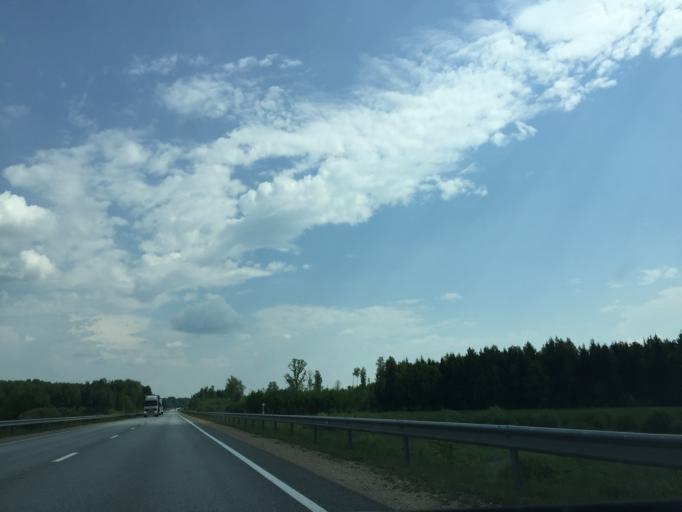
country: LV
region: Lielvarde
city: Lielvarde
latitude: 56.8197
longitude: 24.8039
